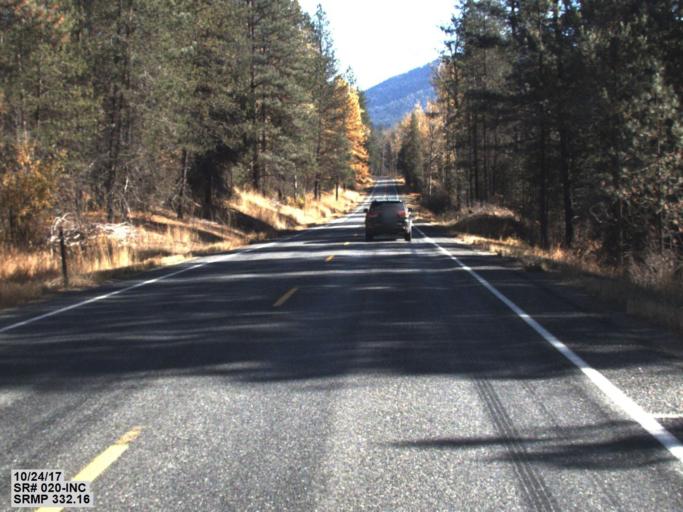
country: US
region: Washington
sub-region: Stevens County
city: Kettle Falls
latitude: 48.5787
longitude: -118.2891
